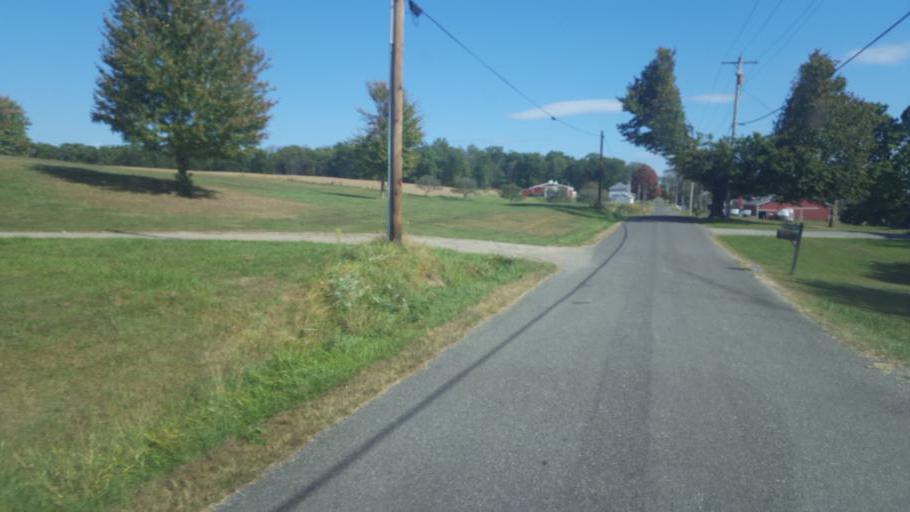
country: US
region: Pennsylvania
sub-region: Mercer County
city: Mercer
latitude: 41.3301
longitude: -80.2688
